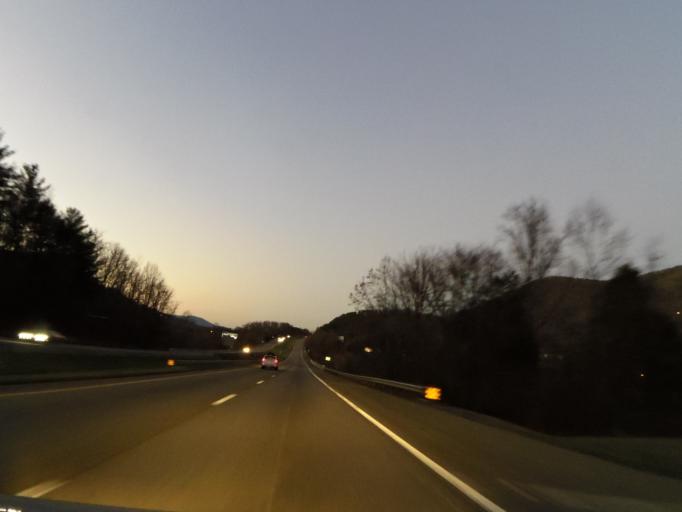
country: US
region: Tennessee
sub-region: Cocke County
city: Newport
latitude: 35.8402
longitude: -83.1810
